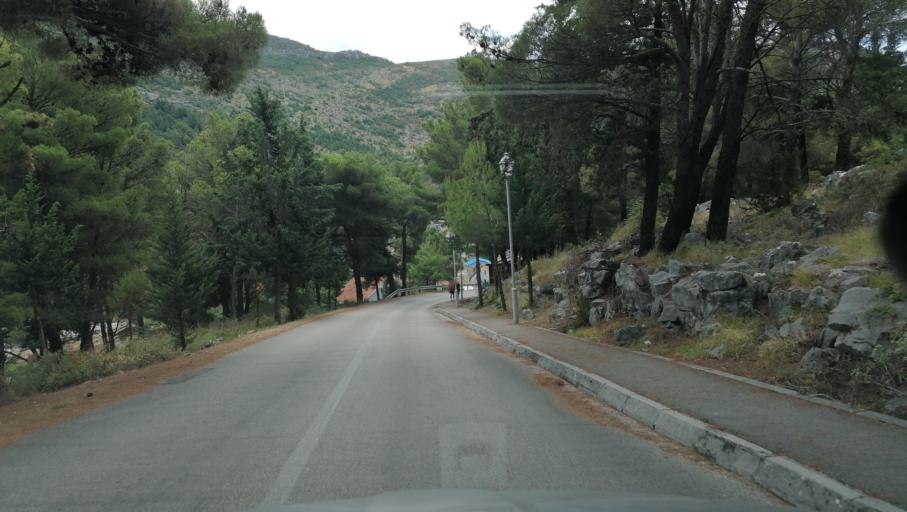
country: BA
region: Republika Srpska
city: Trebinje
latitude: 42.7093
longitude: 18.3623
